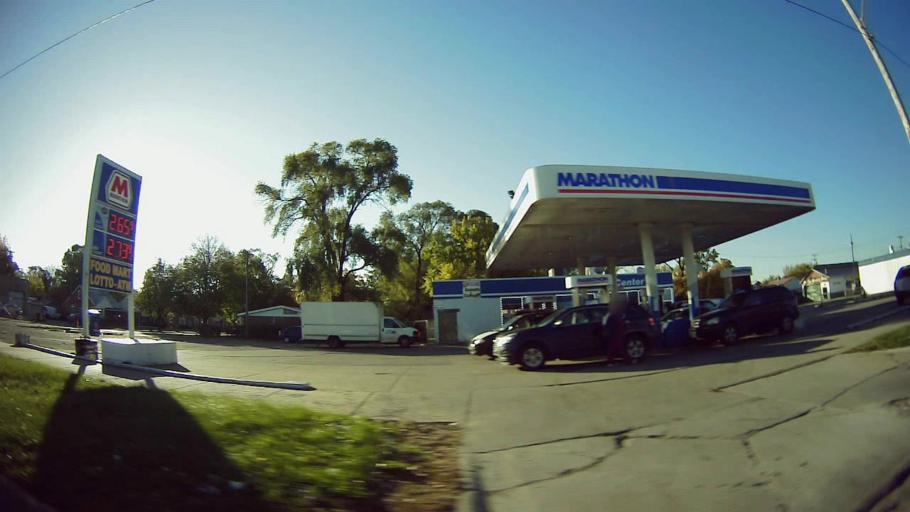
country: US
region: Michigan
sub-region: Oakland County
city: Oak Park
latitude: 42.4453
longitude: -83.1759
